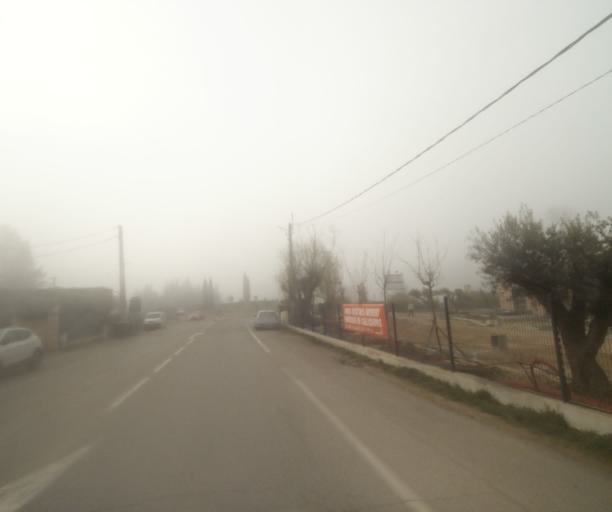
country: FR
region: Provence-Alpes-Cote d'Azur
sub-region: Departement des Bouches-du-Rhone
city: Eguilles
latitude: 43.5430
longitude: 5.3685
